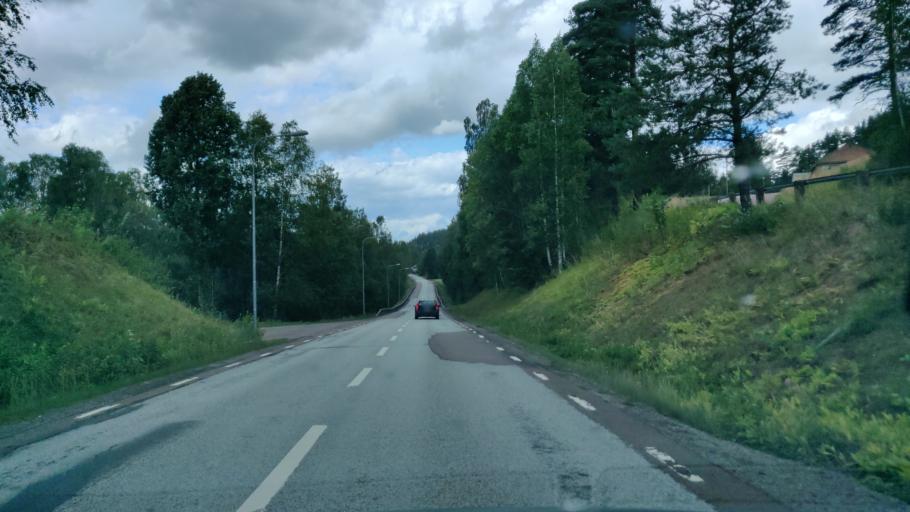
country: SE
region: Vaermland
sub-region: Torsby Kommun
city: Torsby
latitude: 60.6081
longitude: 13.0537
